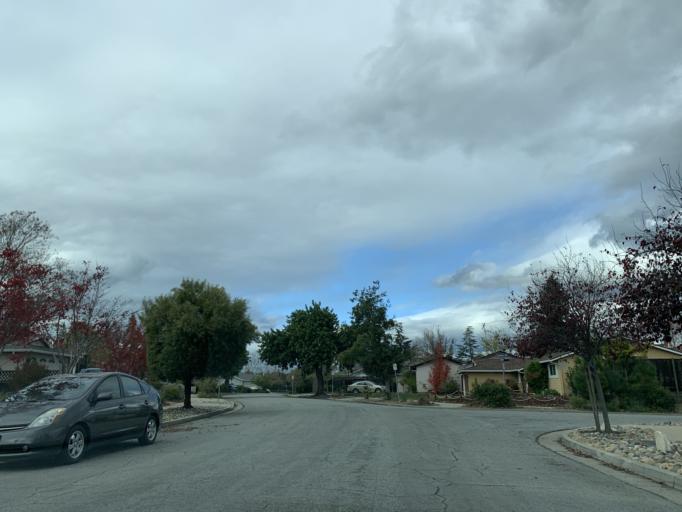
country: US
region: California
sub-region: Santa Clara County
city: Monte Sereno
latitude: 37.2692
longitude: -121.9851
